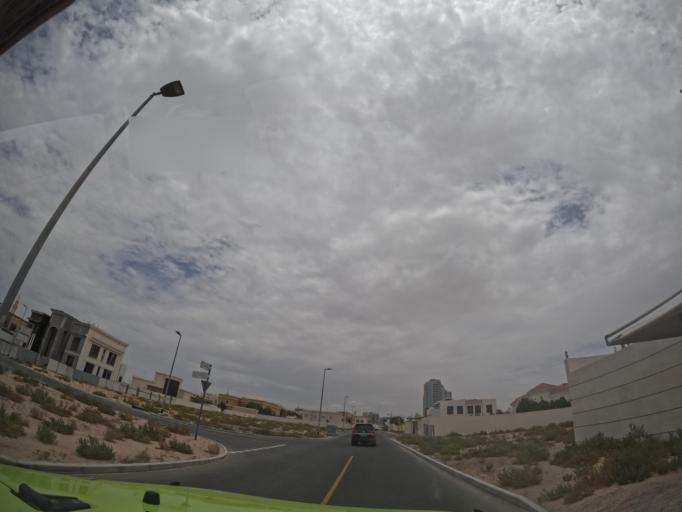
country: AE
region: Dubai
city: Dubai
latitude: 25.1280
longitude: 55.3694
